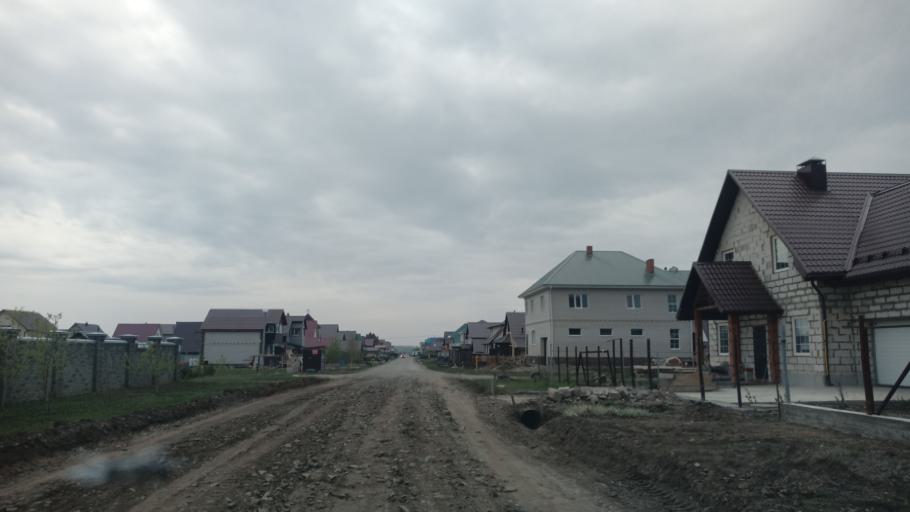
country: RU
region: Altai Krai
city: Yuzhnyy
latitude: 53.2256
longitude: 83.6908
